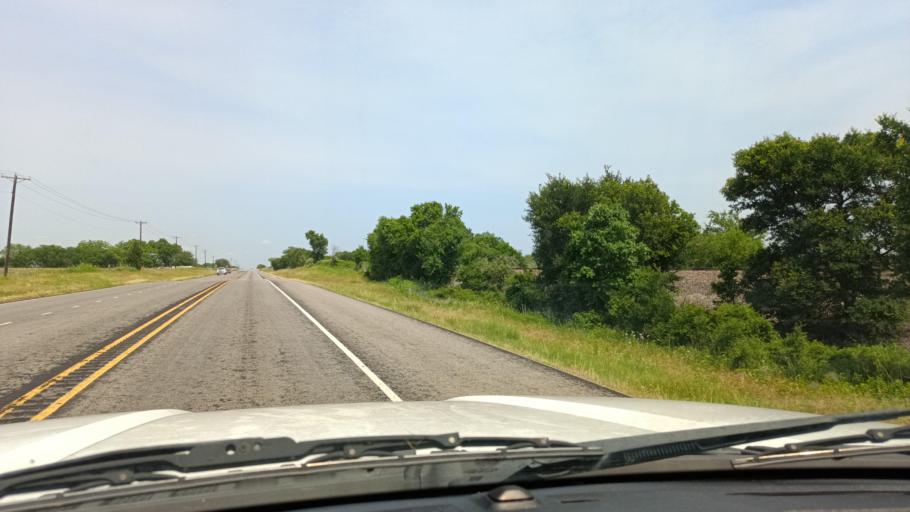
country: US
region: Texas
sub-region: Milam County
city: Cameron
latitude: 30.8488
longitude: -97.0611
